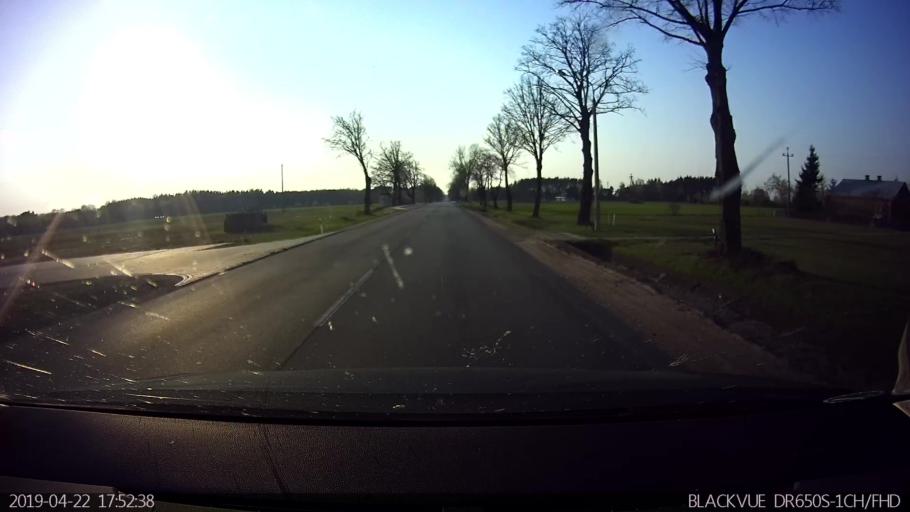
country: PL
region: Masovian Voivodeship
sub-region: Powiat wegrowski
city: Wegrow
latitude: 52.4451
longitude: 21.9716
